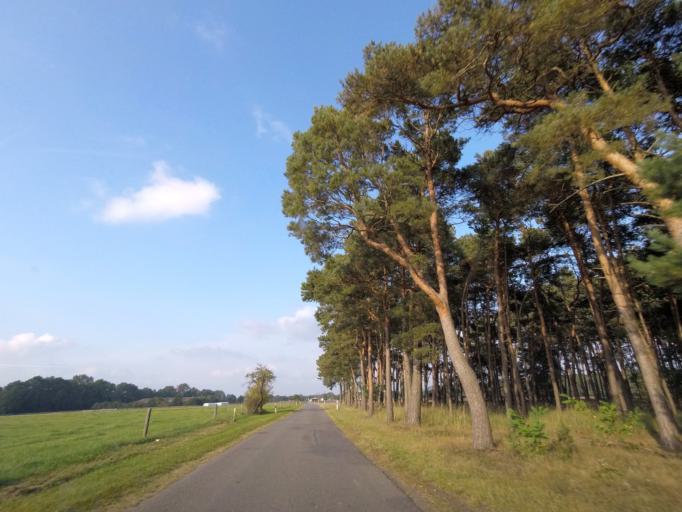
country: DE
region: Brandenburg
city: Linthe
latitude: 52.1457
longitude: 12.7225
